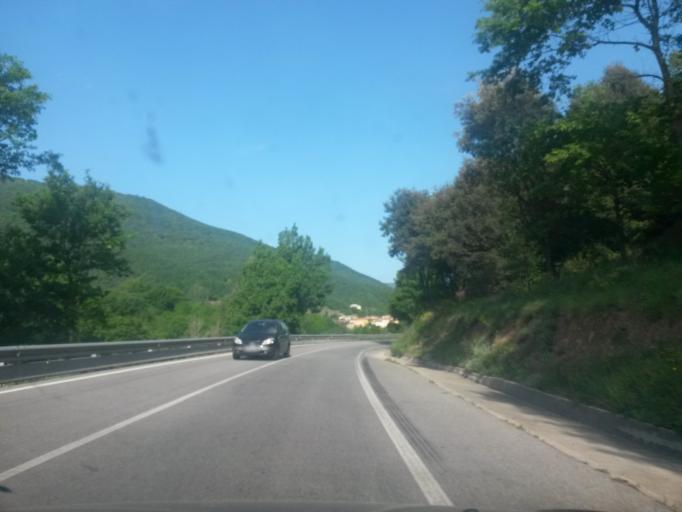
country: ES
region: Catalonia
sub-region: Provincia de Girona
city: Sant Feliu de Pallerols
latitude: 42.0725
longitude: 2.5175
